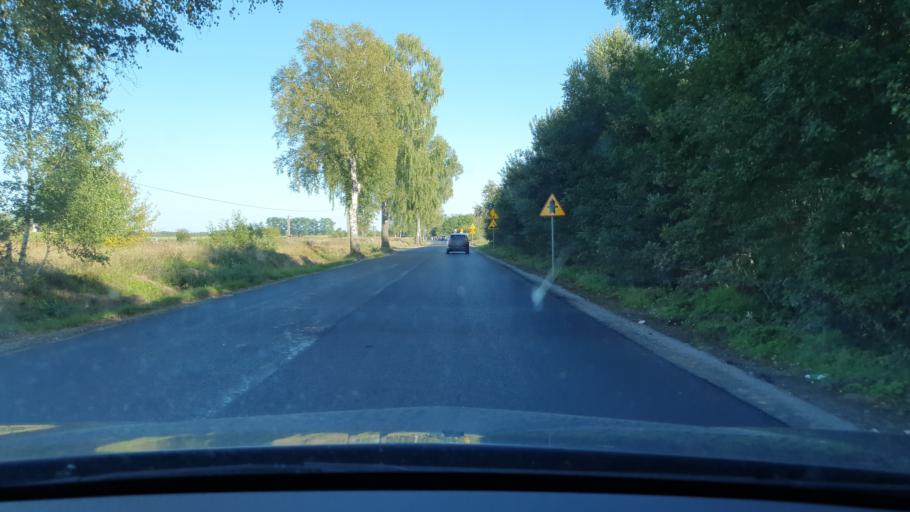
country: PL
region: West Pomeranian Voivodeship
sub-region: Powiat gryficki
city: Ploty
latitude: 53.8110
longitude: 15.2022
